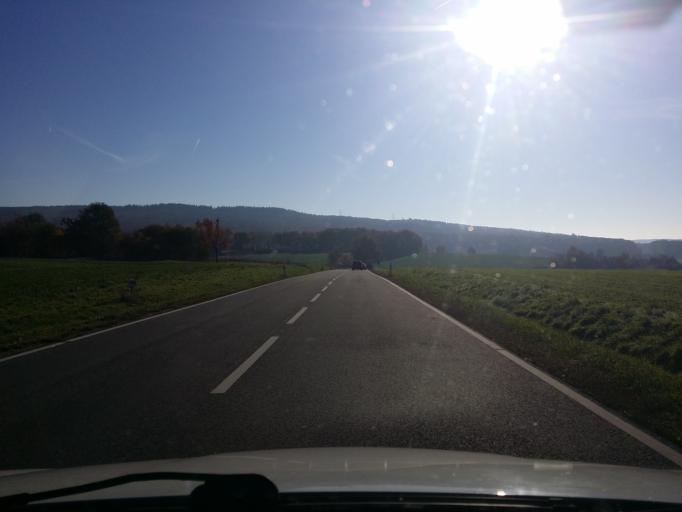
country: DE
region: Hesse
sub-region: Regierungsbezirk Darmstadt
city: Idstein
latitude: 50.1923
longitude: 8.2887
